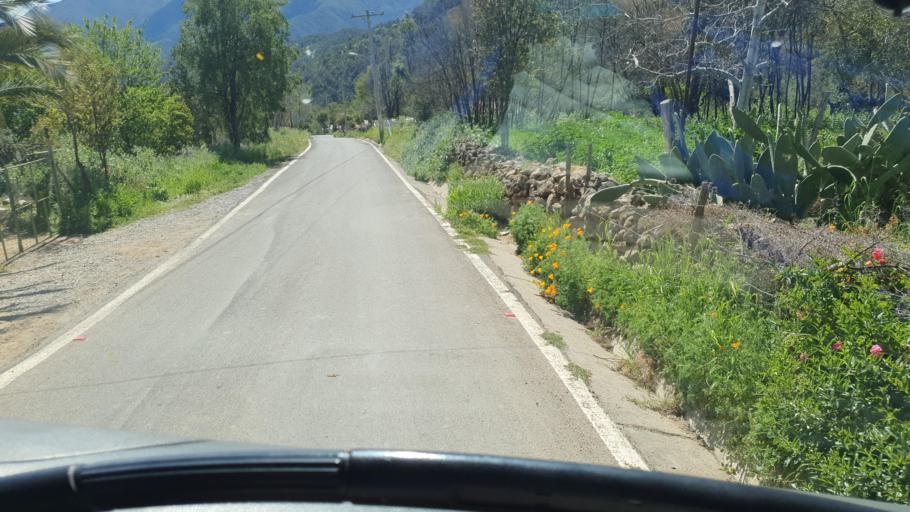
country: CL
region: Santiago Metropolitan
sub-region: Provincia de Chacabuco
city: Lampa
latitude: -33.1932
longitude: -71.0961
